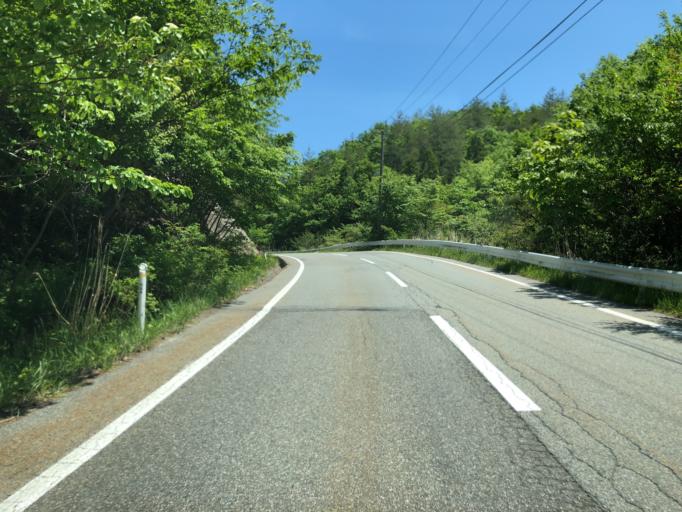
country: JP
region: Fukushima
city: Namie
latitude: 37.5213
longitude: 140.7884
